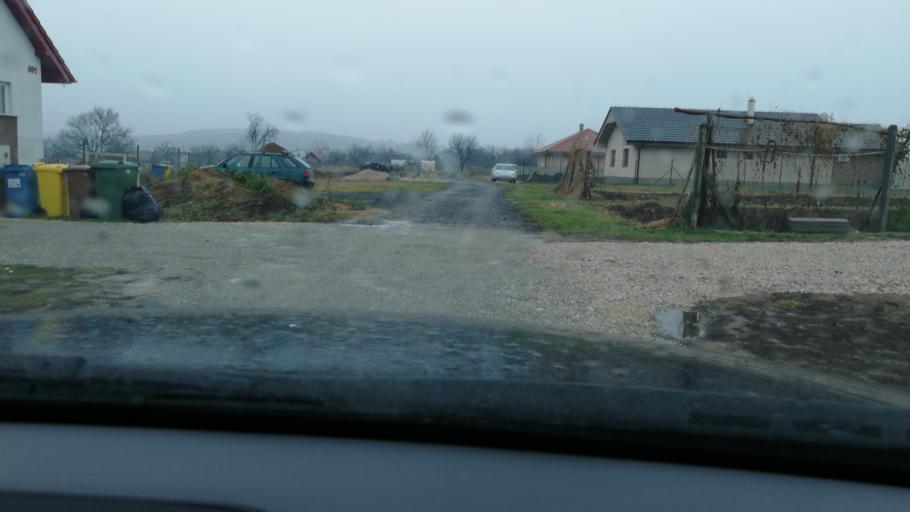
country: SK
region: Nitriansky
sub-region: Okres Nitra
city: Nitra
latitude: 48.3161
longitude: 17.9861
